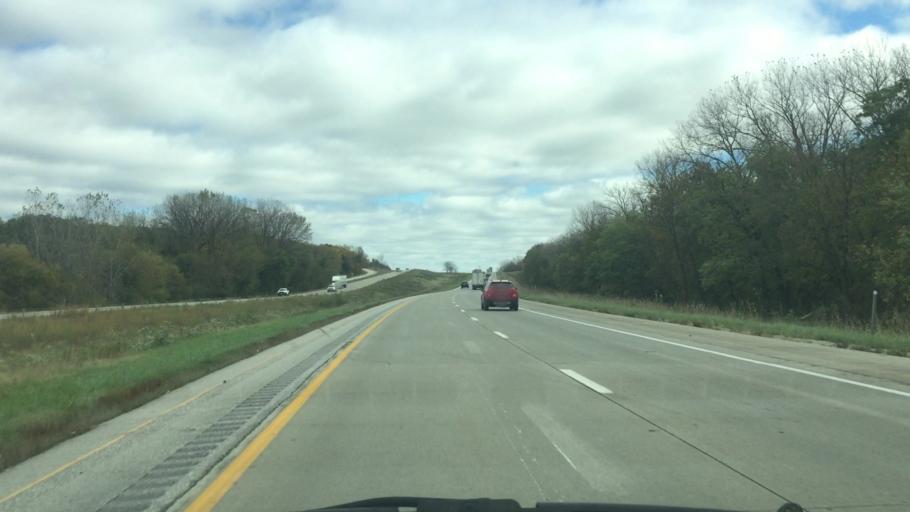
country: US
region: Iowa
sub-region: Jasper County
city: Colfax
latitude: 41.6849
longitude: -93.2877
